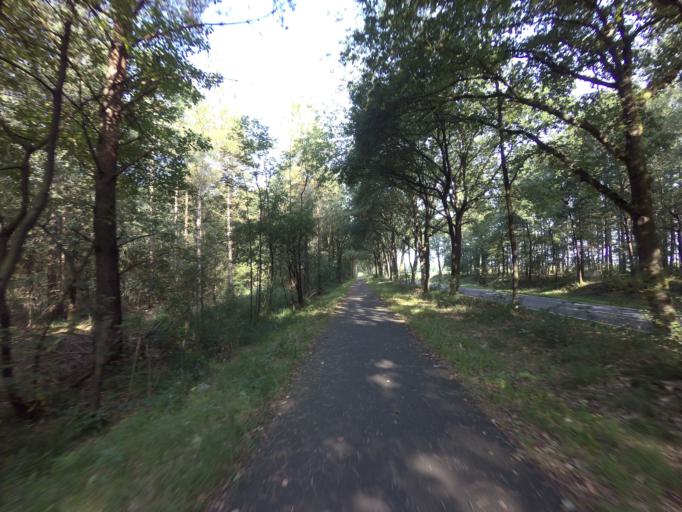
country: DE
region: Lower Saxony
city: Wielen
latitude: 52.5423
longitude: 6.6982
